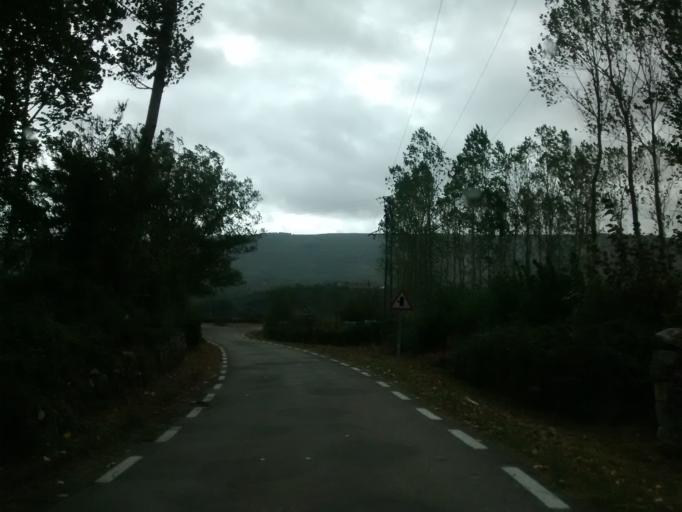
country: ES
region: Castille and Leon
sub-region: Provincia de Palencia
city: Berzosilla
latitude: 42.7946
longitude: -3.9657
